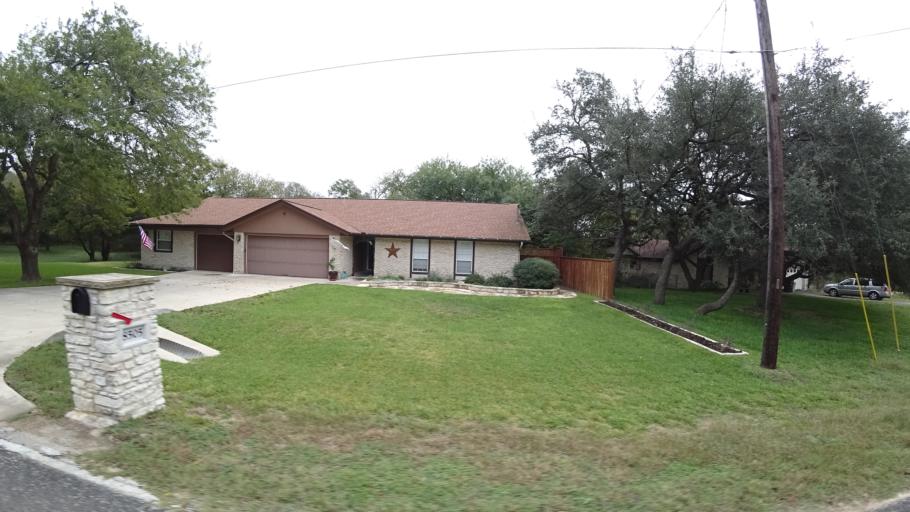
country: US
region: Texas
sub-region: Travis County
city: Barton Creek
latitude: 30.2264
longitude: -97.8960
